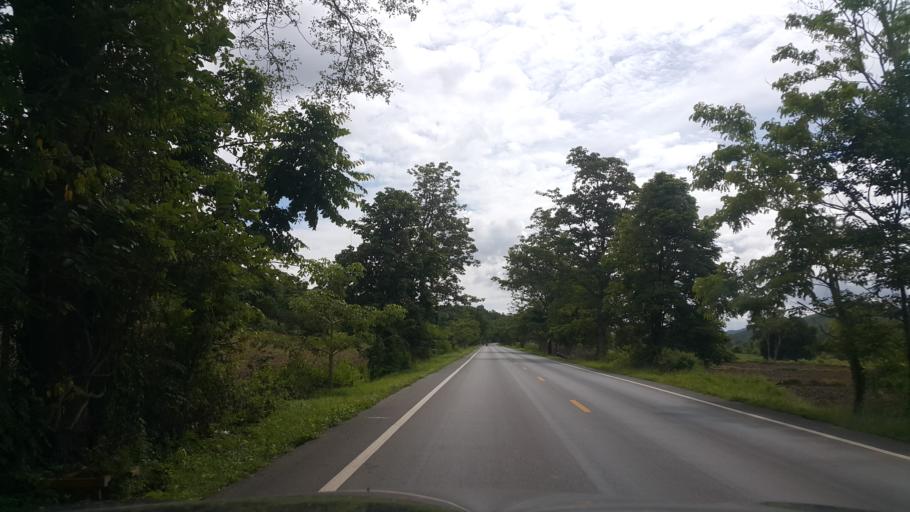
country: TH
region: Uttaradit
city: Thong Saen Khan
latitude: 17.3672
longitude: 100.2508
